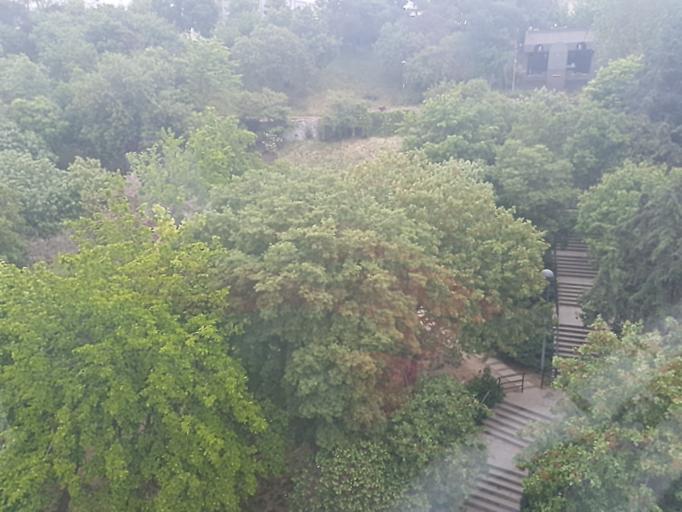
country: TR
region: Istanbul
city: Sisli
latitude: 41.0442
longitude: 28.9930
